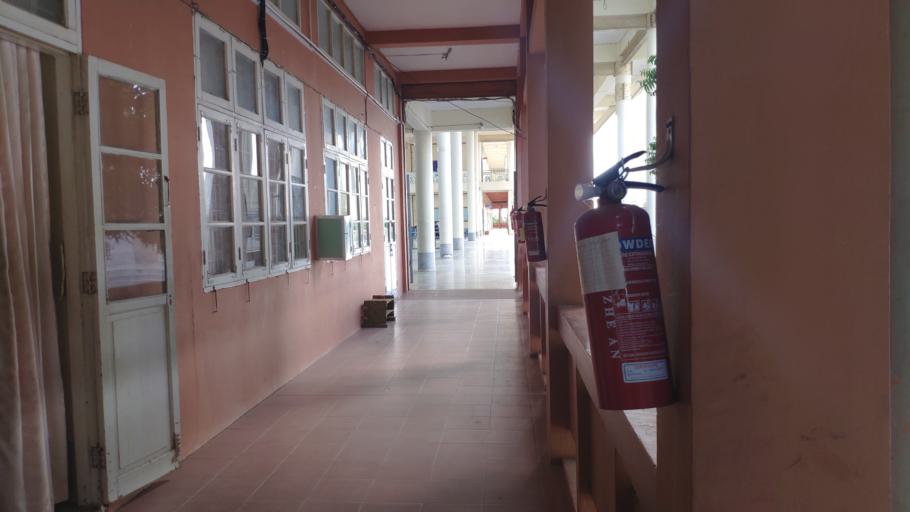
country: MM
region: Mandalay
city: Meiktila
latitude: 20.9136
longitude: 95.8592
